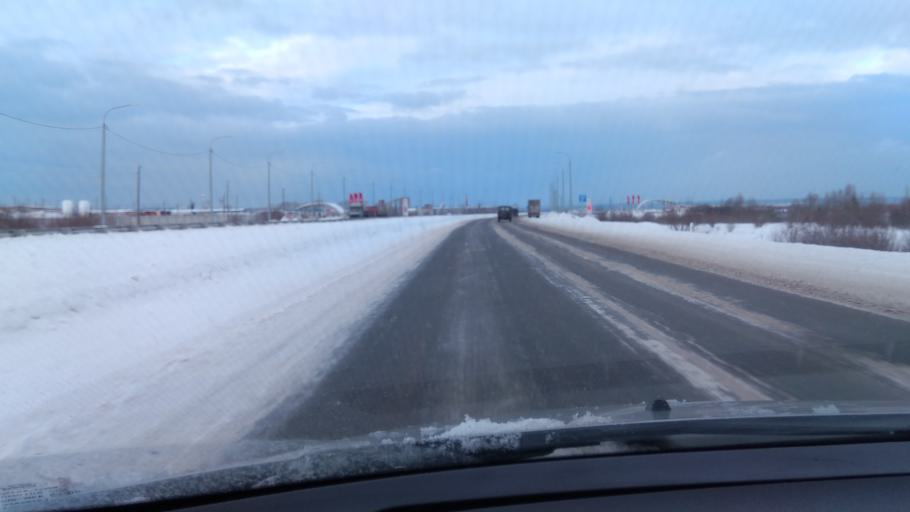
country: RU
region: Sverdlovsk
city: Tsementnyy
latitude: 57.4645
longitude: 60.1863
